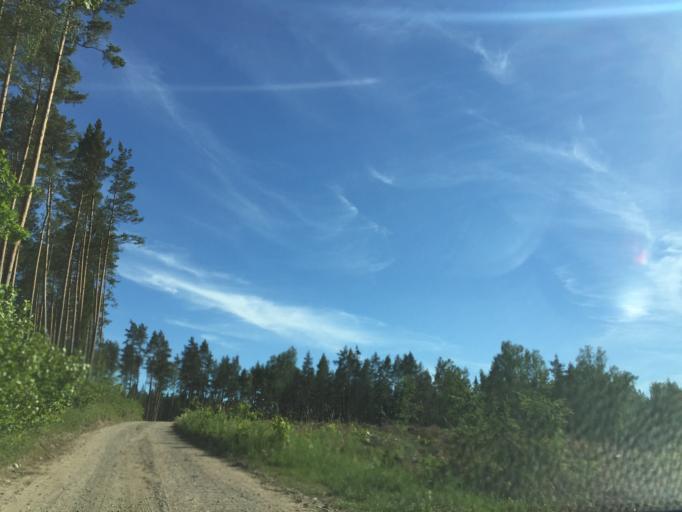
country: LV
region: Kuldigas Rajons
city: Kuldiga
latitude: 57.0674
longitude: 21.8245
